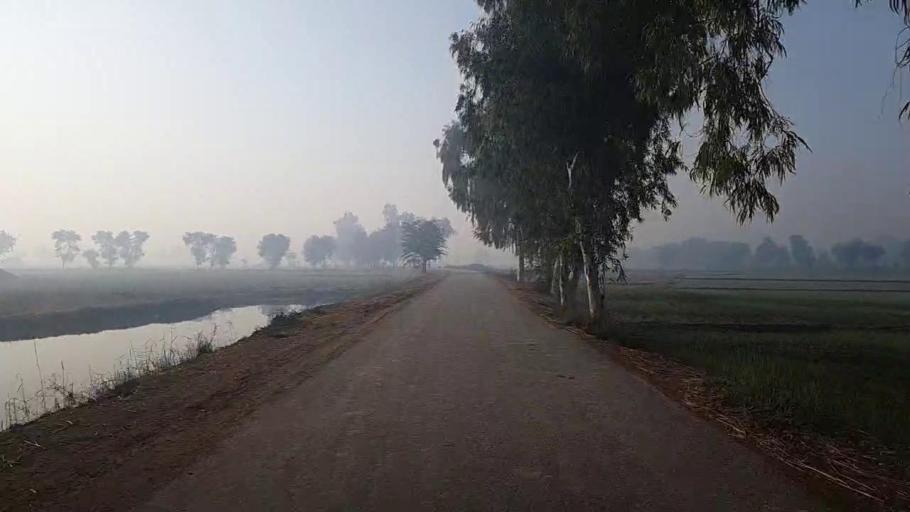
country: PK
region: Sindh
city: Mehar
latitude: 27.1447
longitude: 67.8228
